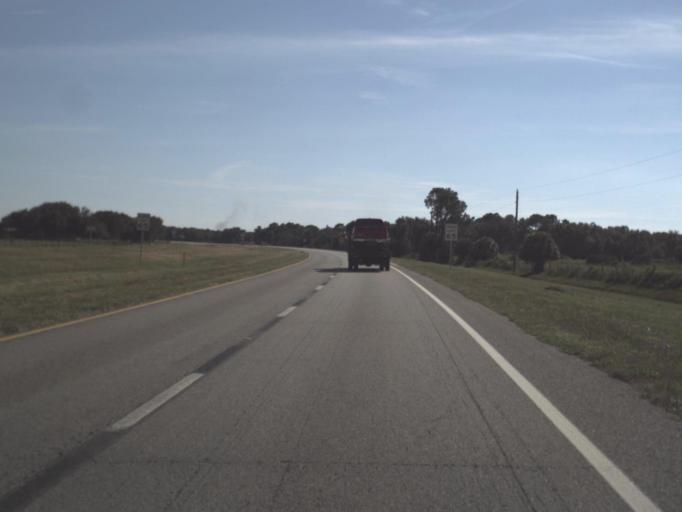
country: US
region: Florida
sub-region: Highlands County
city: Placid Lakes
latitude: 27.0355
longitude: -81.3426
